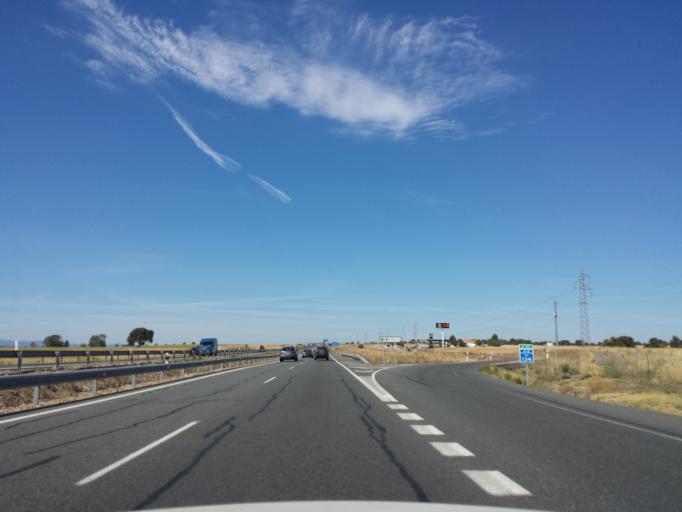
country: ES
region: Castille-La Mancha
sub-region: Province of Toledo
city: Calera y Chozas
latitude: 39.9270
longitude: -5.0213
